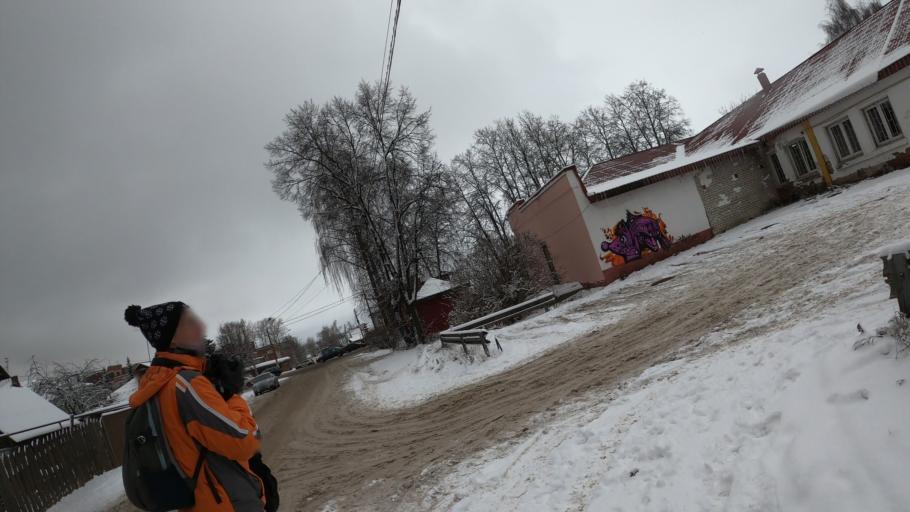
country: RU
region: Jaroslavl
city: Pereslavl'-Zalesskiy
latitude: 56.7434
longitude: 38.8579
